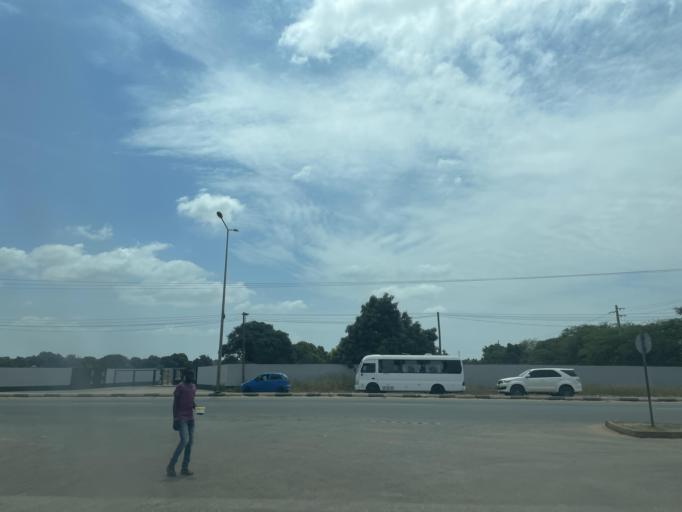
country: AO
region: Luanda
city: Luanda
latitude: -8.9616
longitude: 13.3893
